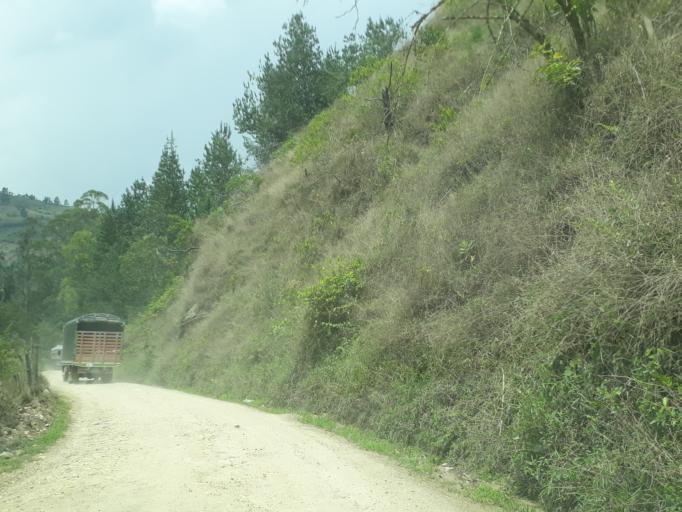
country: CO
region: Cundinamarca
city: Macheta
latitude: 5.0803
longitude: -73.5803
